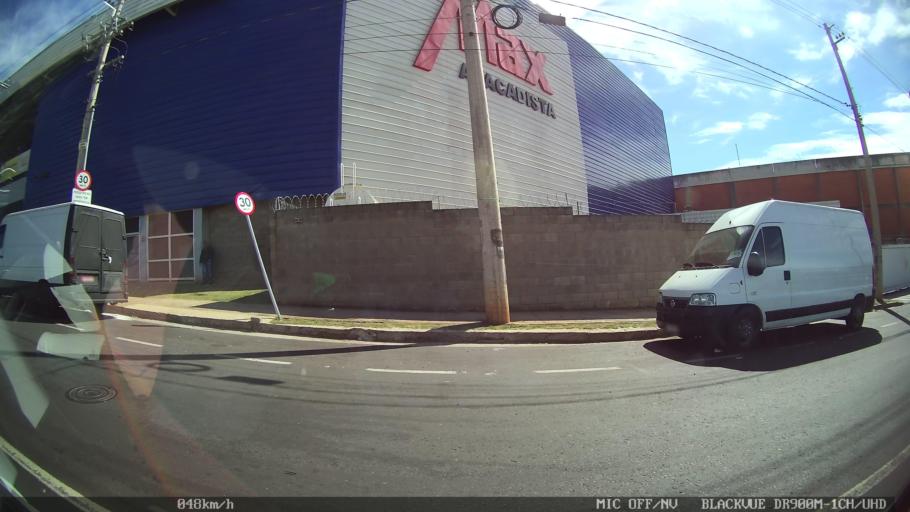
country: BR
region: Sao Paulo
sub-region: Sao Jose Do Rio Preto
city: Sao Jose do Rio Preto
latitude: -20.8395
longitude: -49.3693
